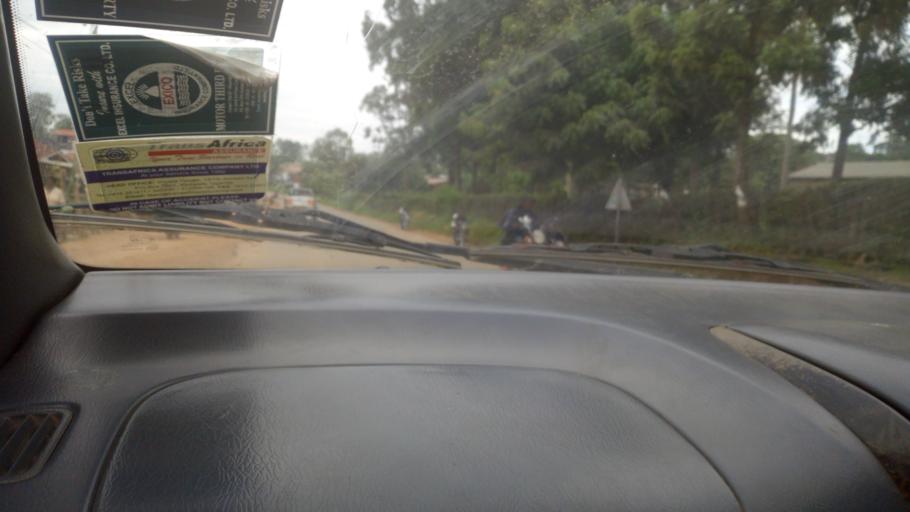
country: UG
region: Western Region
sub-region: Mbarara District
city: Mbarara
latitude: -0.6039
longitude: 30.6526
